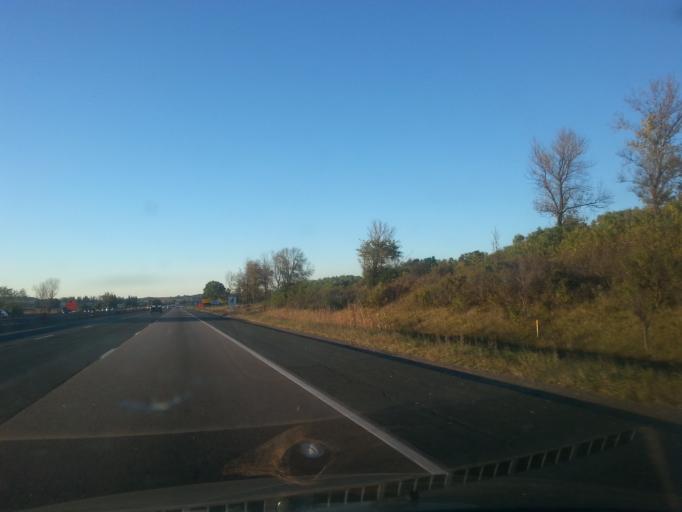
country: CA
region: Ontario
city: Bradford West Gwillimbury
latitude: 44.0574
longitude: -79.6135
